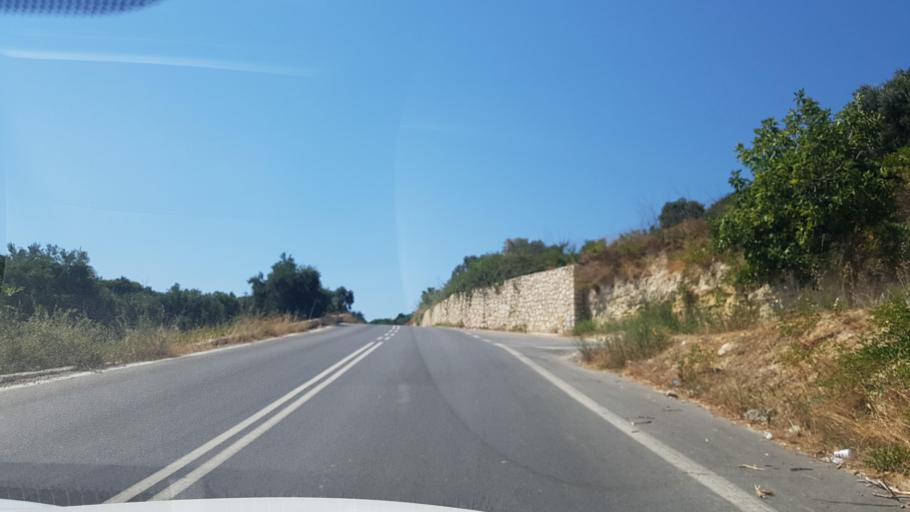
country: GR
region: Crete
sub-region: Nomos Rethymnis
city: Panormos
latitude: 35.3805
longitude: 24.5959
